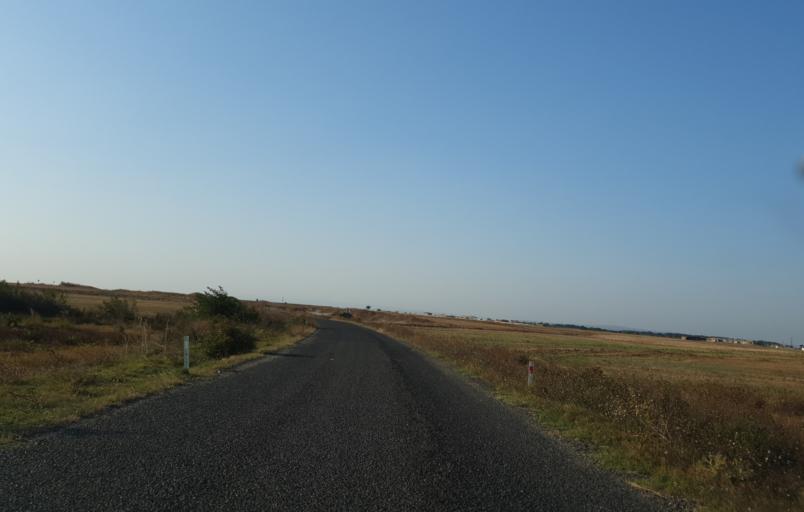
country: TR
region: Tekirdag
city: Beyazkoy
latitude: 41.4180
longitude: 27.7643
